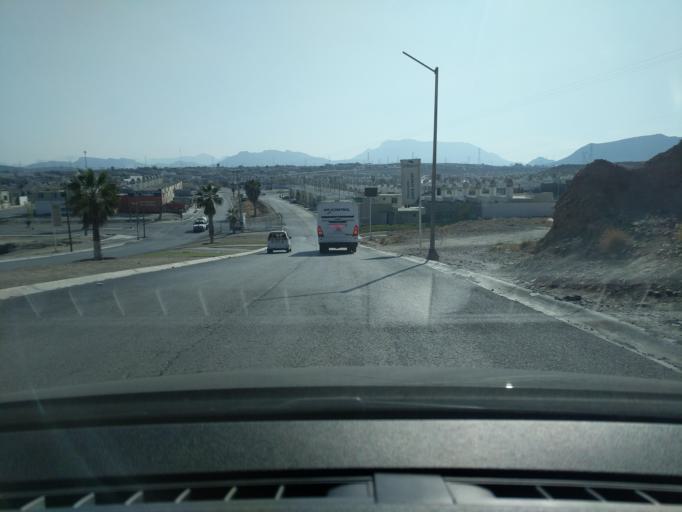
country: MX
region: Coahuila
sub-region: Ramos Arizpe
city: Ramos Arizpe
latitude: 25.5534
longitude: -100.9636
